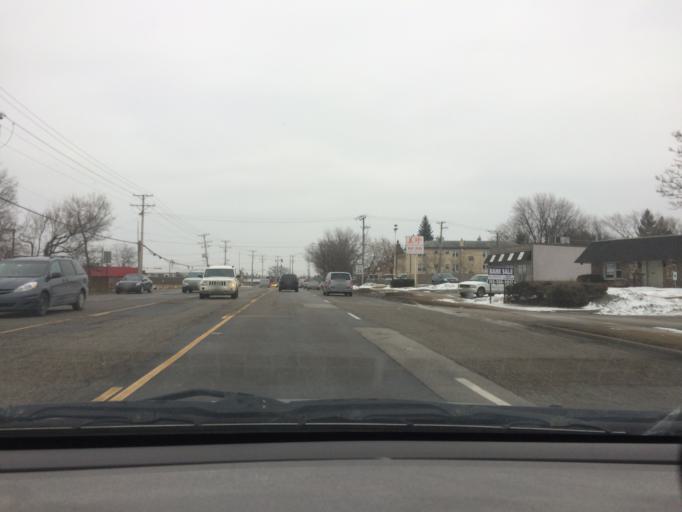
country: US
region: Illinois
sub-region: DuPage County
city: Hanover Park
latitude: 42.0073
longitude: -88.1506
